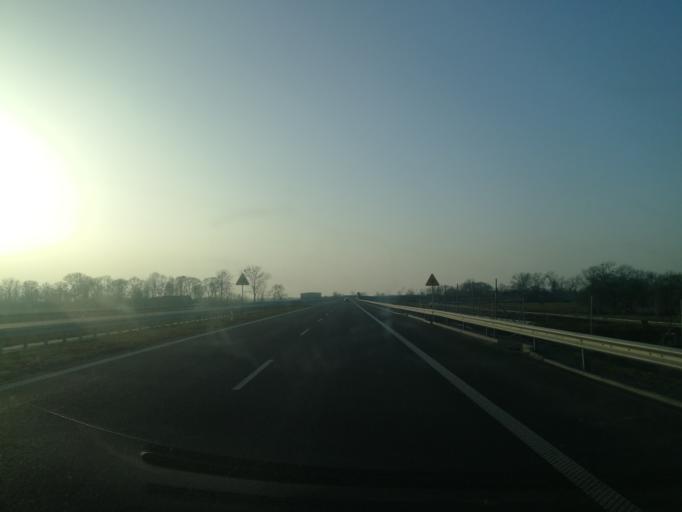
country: PL
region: Pomeranian Voivodeship
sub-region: Powiat nowodworski
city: Nowy Dwor Gdanski
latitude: 54.1733
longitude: 19.2057
